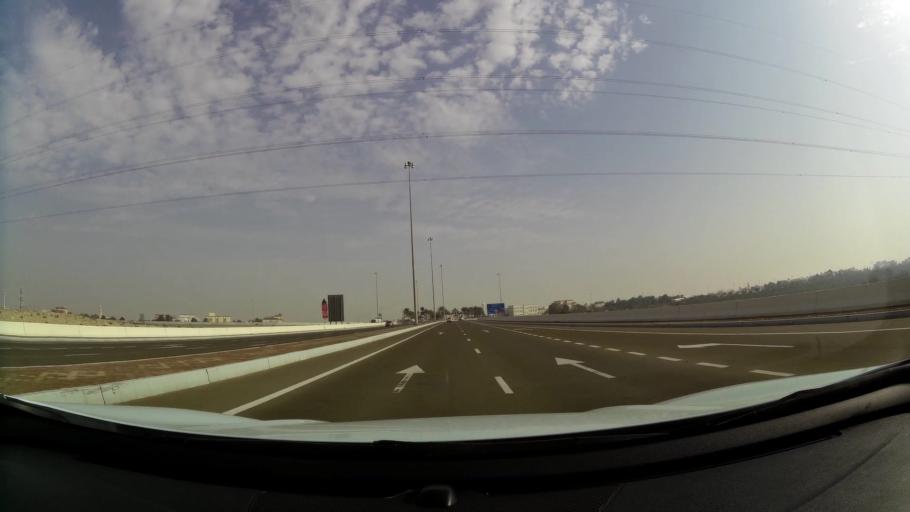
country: AE
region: Abu Dhabi
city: Abu Dhabi
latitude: 24.2537
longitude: 54.7093
